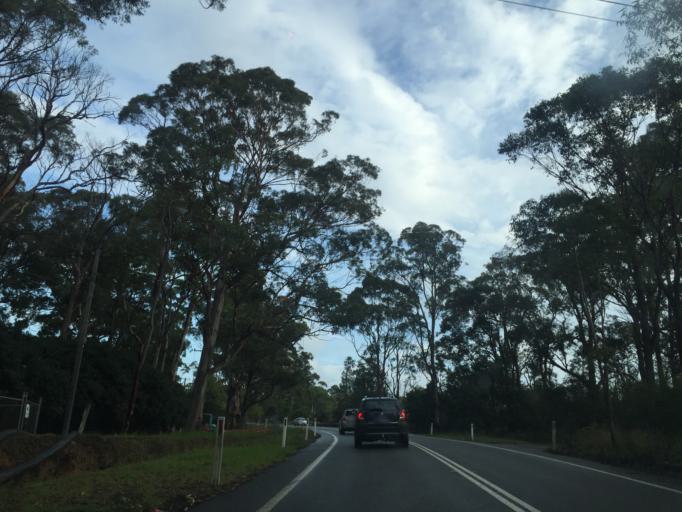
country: AU
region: New South Wales
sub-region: Hornsby Shire
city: Galston
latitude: -33.6656
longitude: 151.0378
